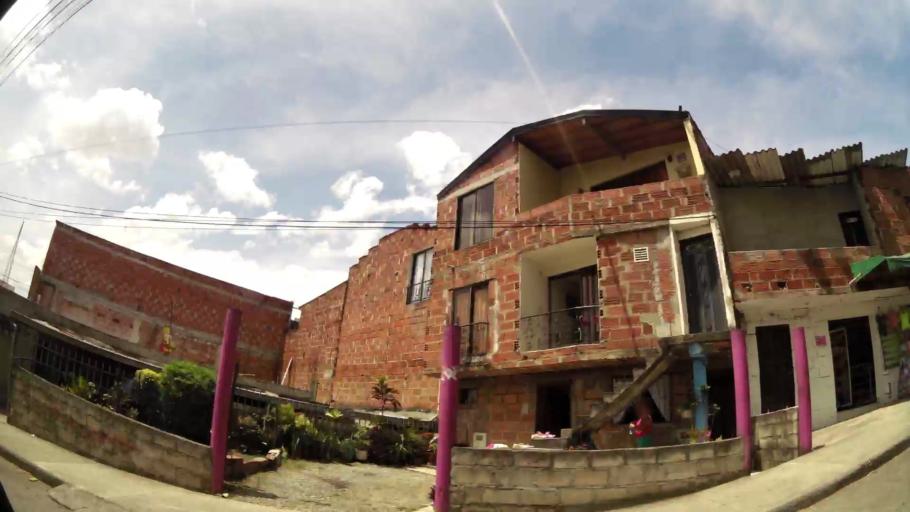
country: CO
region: Antioquia
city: Bello
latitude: 6.3453
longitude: -75.5500
